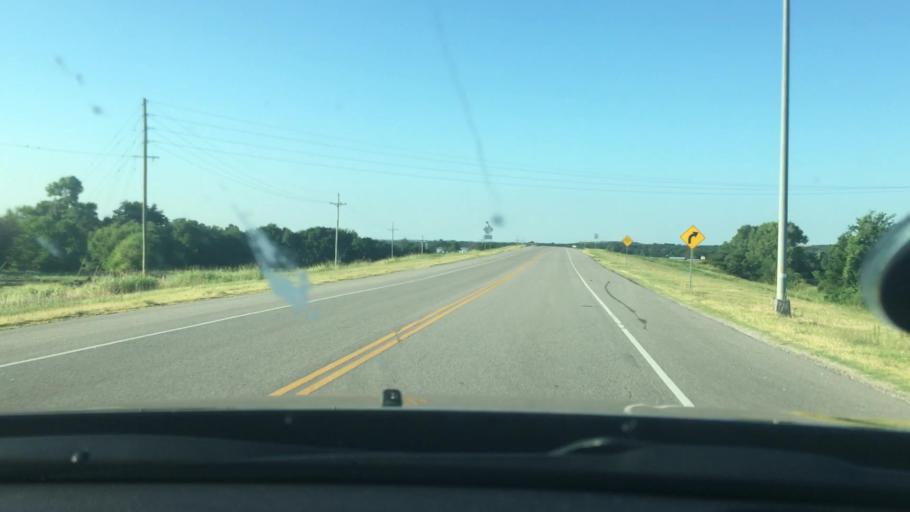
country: US
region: Oklahoma
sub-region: Pontotoc County
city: Ada
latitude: 34.6559
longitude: -96.7954
